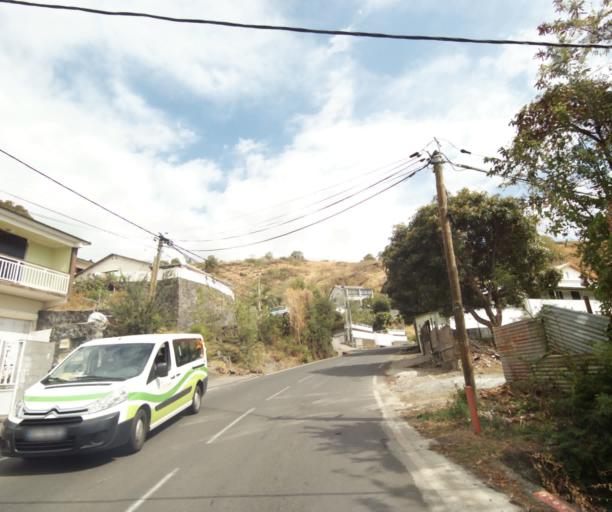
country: RE
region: Reunion
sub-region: Reunion
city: Saint-Paul
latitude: -21.0154
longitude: 55.2786
